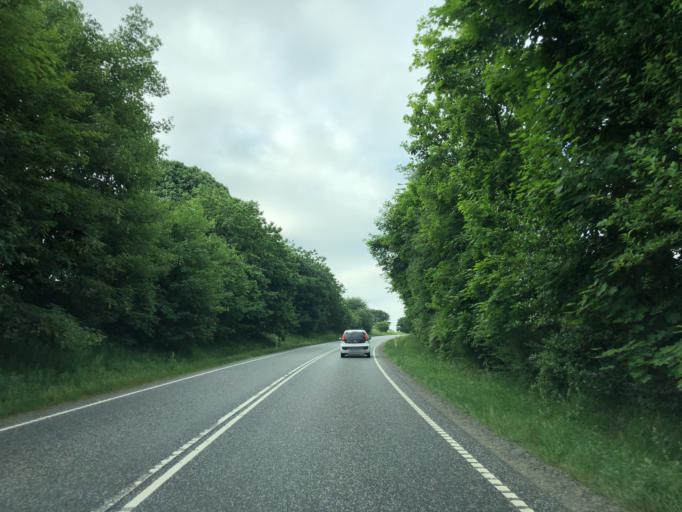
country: DK
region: South Denmark
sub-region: Vejle Kommune
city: Give
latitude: 55.7697
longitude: 9.2891
